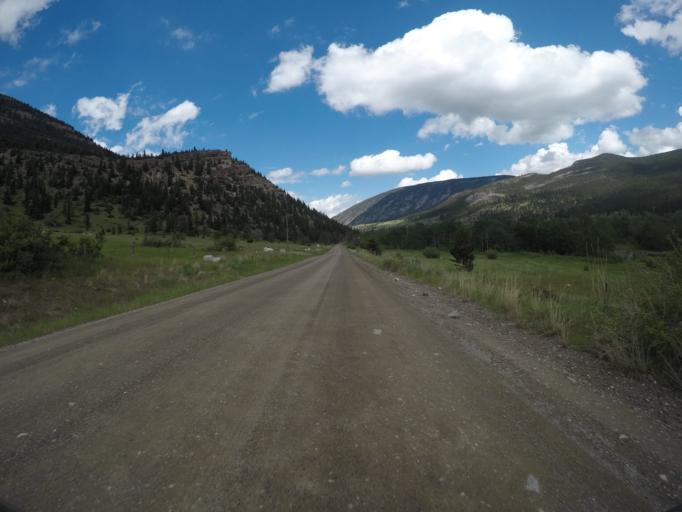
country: US
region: Montana
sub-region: Park County
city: Livingston
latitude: 45.5291
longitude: -110.2170
